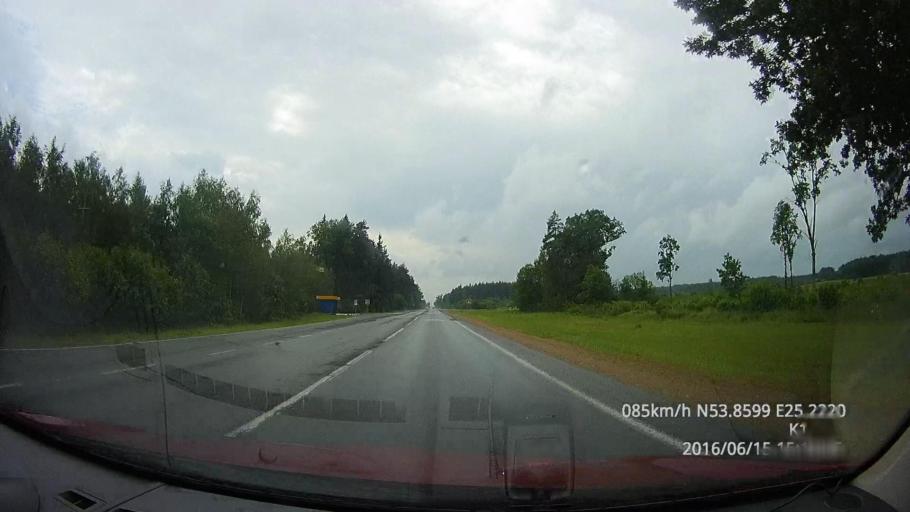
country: BY
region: Grodnenskaya
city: Lida
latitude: 53.8598
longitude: 25.2217
